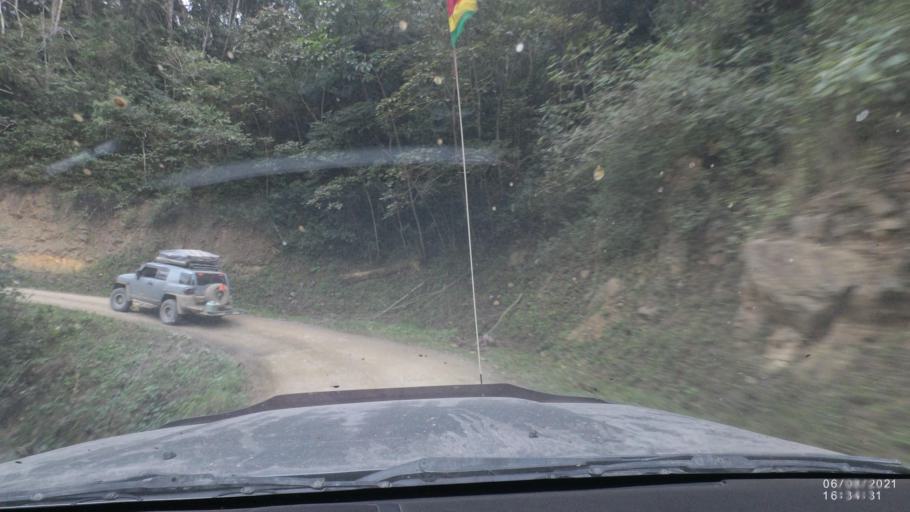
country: BO
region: La Paz
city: Quime
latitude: -16.5256
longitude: -66.7661
